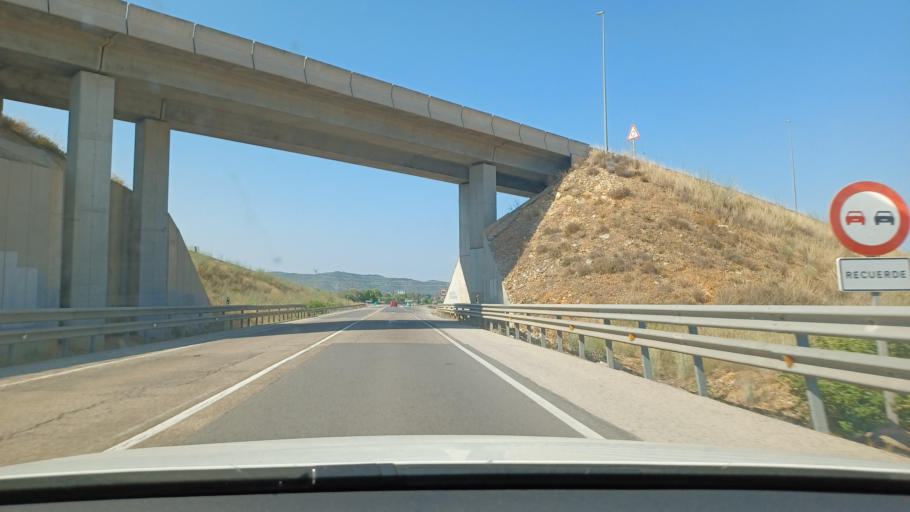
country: ES
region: Valencia
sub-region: Provincia de Castello
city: Alcala de Xivert
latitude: 40.3122
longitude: 0.2326
